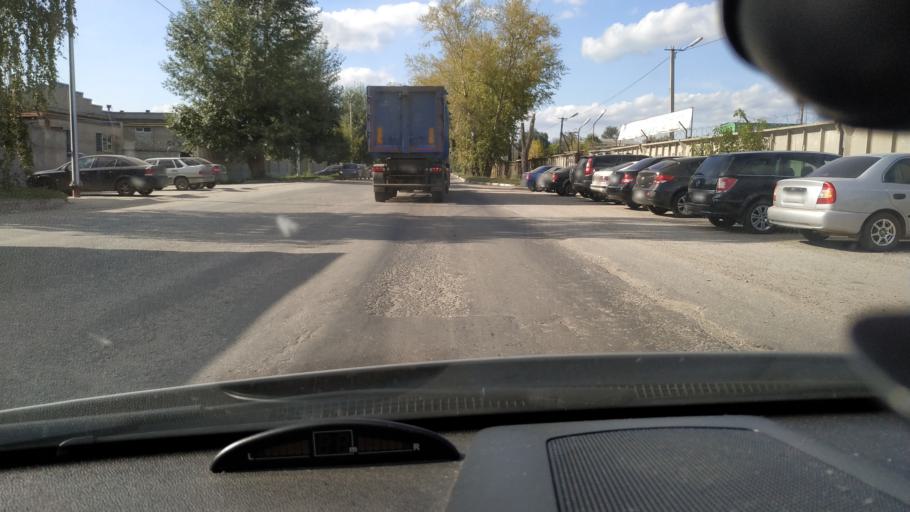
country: RU
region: Rjazan
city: Ryazan'
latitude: 54.6561
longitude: 39.6378
